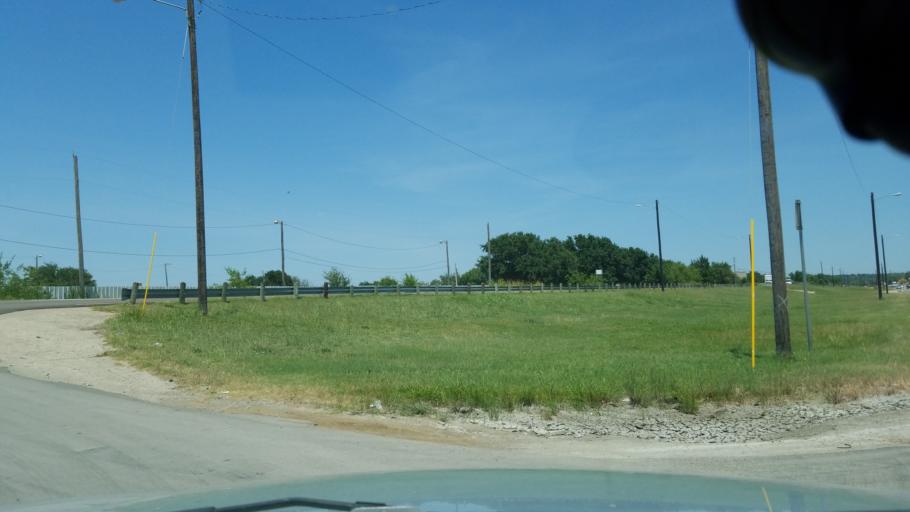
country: US
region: Texas
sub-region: Dallas County
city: Grand Prairie
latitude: 32.7464
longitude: -96.9480
